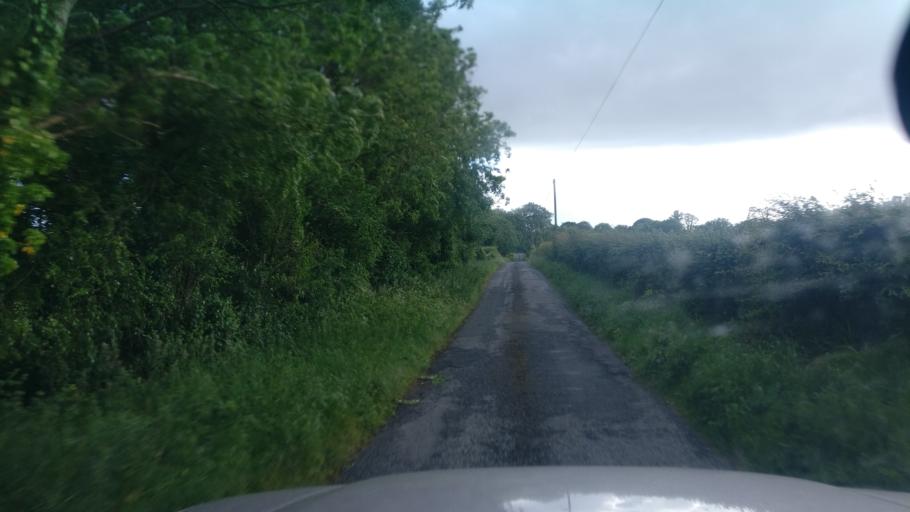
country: IE
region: Connaught
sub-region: County Galway
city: Ballinasloe
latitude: 53.2295
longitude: -8.2230
